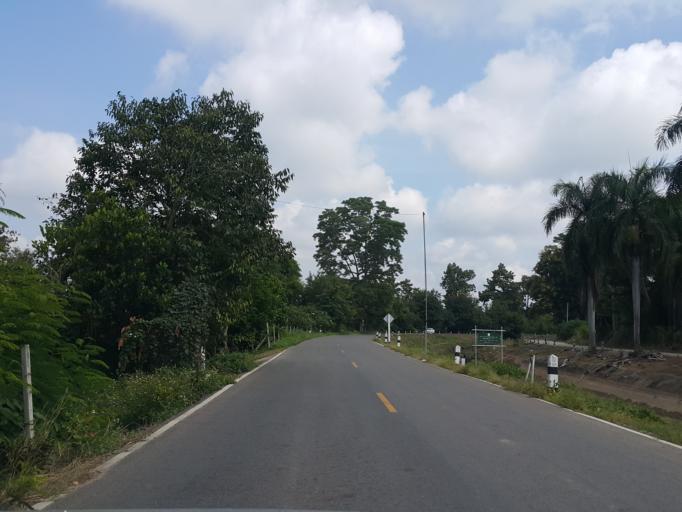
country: TH
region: Chiang Mai
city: San Sai
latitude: 18.9132
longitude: 99.0114
